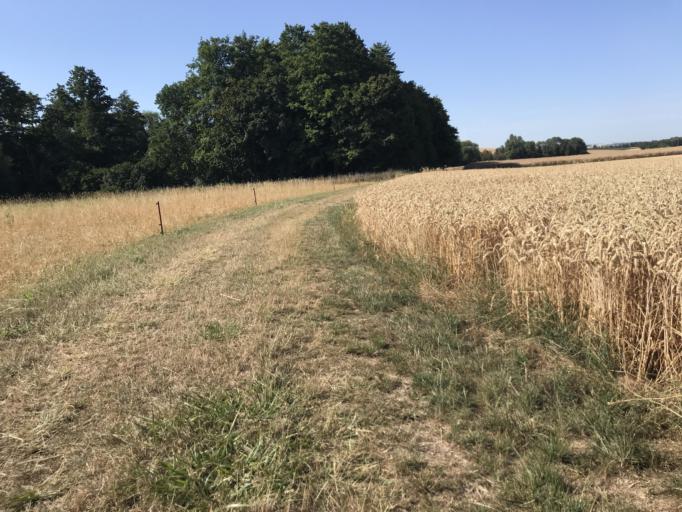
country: DE
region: Rheinland-Pfalz
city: Klein-Winternheim
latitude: 49.9293
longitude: 8.2190
